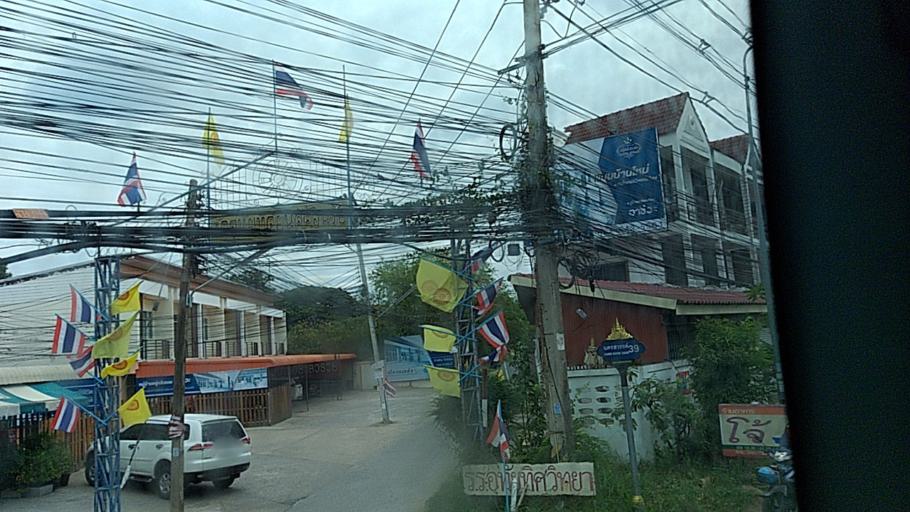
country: TH
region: Maha Sarakham
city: Maha Sarakham
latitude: 16.1765
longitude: 103.3141
